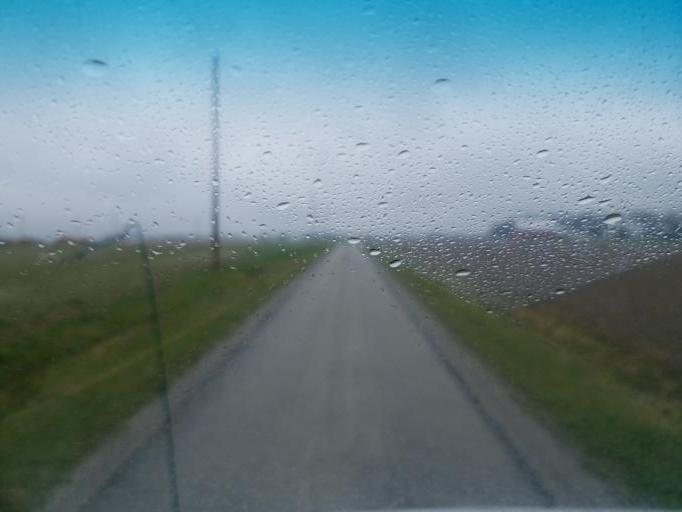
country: US
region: Ohio
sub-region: Crawford County
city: Bucyrus
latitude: 40.9489
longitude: -82.9972
